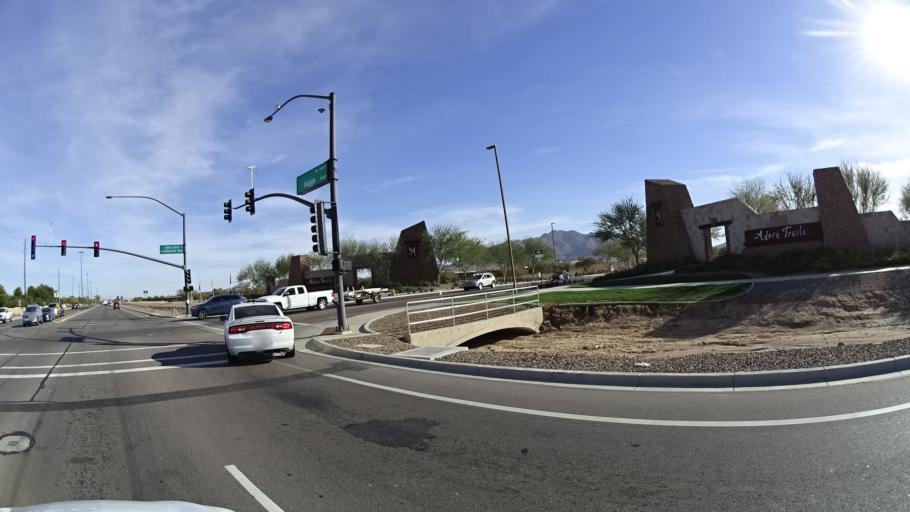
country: US
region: Arizona
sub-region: Maricopa County
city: Queen Creek
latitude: 33.2193
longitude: -111.7345
